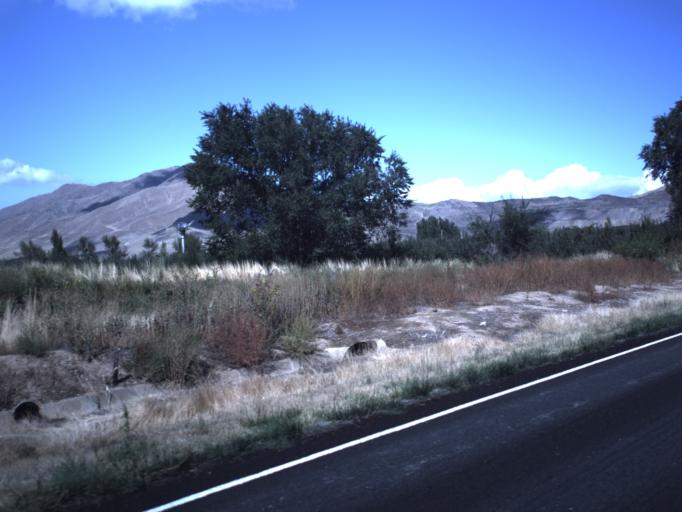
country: US
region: Utah
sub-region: Utah County
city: Genola
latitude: 39.9945
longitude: -111.8273
